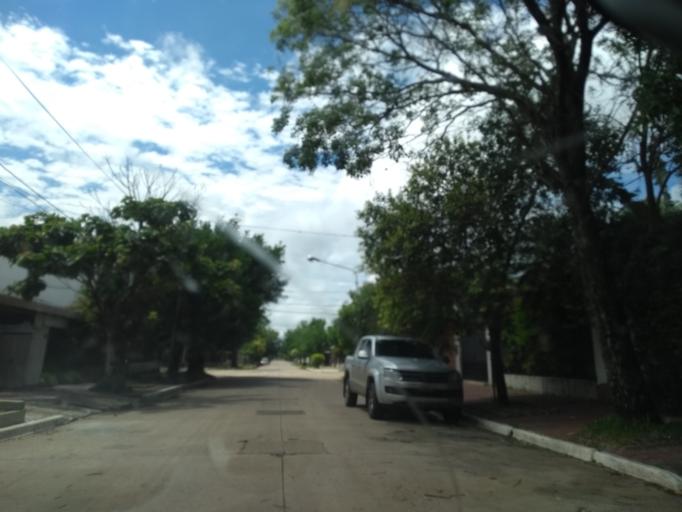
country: AR
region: Chaco
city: Barranqueras
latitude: -27.4789
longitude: -58.9540
